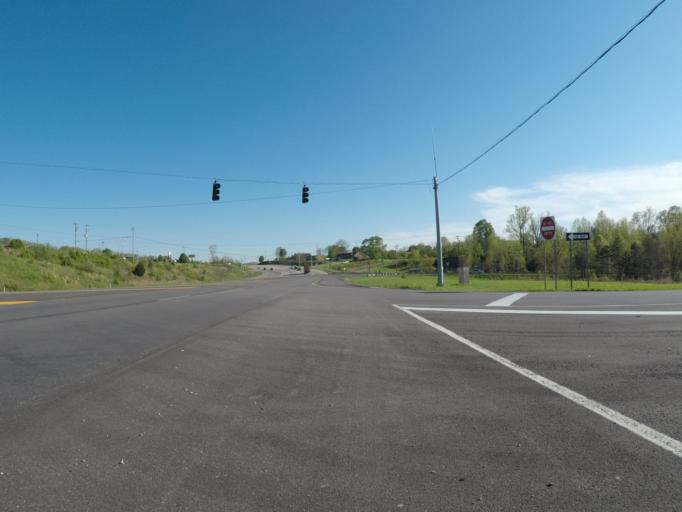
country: US
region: Kentucky
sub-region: Boyd County
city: Meads
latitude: 38.3668
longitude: -82.6989
